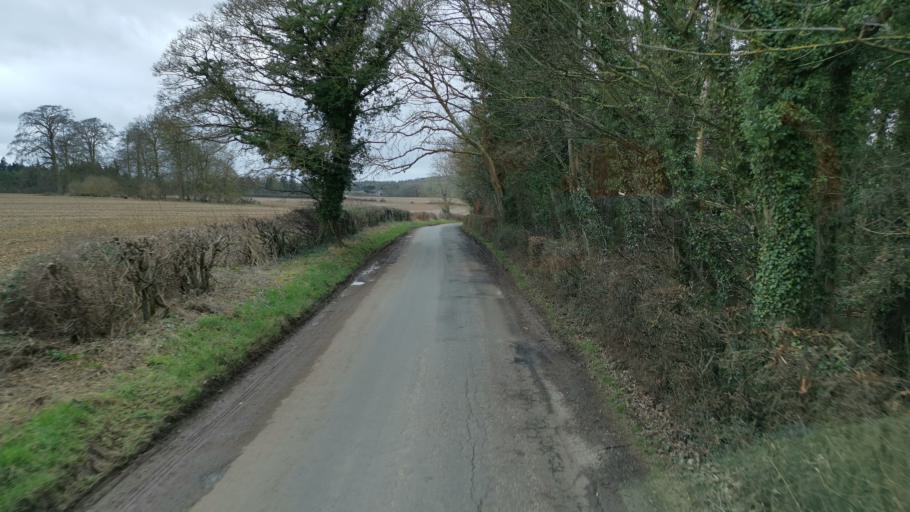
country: GB
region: England
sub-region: Oxfordshire
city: Somerton
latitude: 51.9007
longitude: -1.3102
